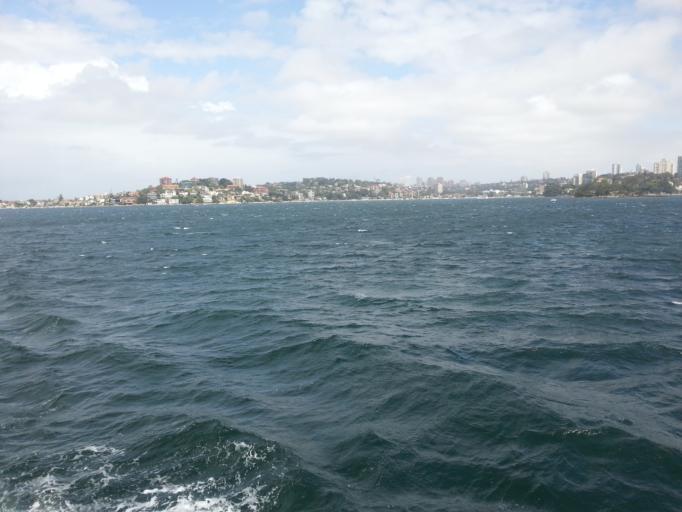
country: AU
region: New South Wales
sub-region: Woollahra
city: Point Piper
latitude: -33.8546
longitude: 151.2427
